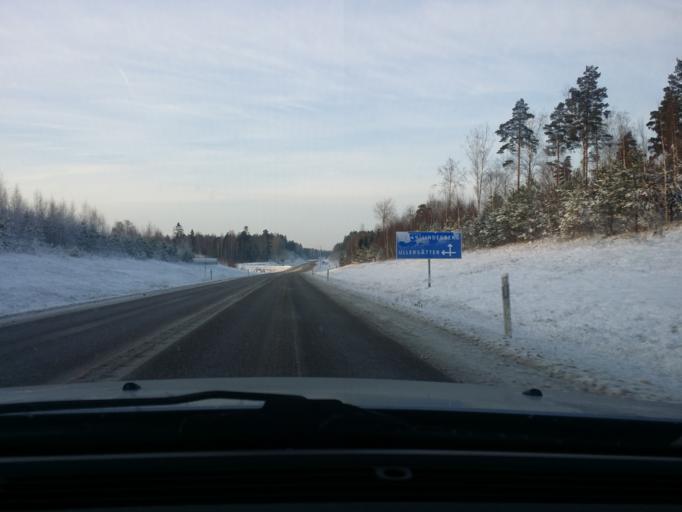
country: SE
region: OErebro
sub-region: Lindesbergs Kommun
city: Fellingsbro
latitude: 59.4601
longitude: 15.4773
